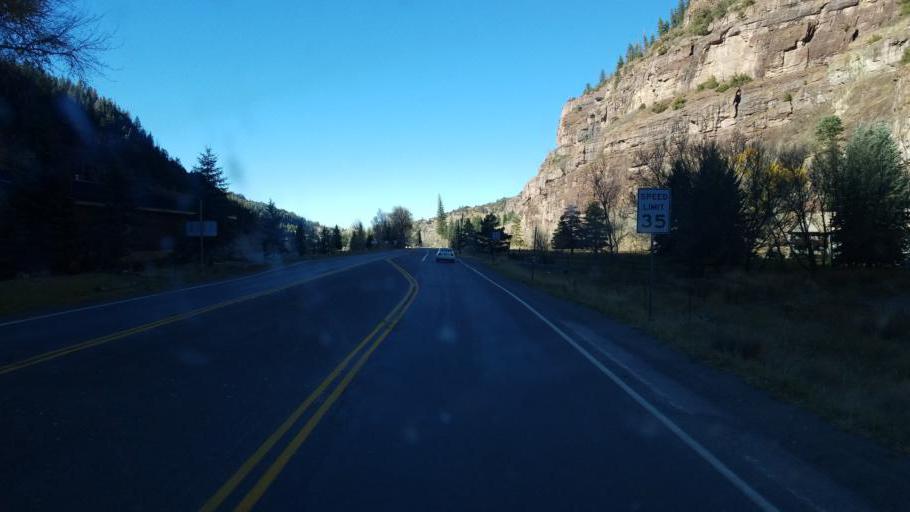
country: US
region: Colorado
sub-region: Ouray County
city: Ouray
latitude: 38.0382
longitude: -107.6787
